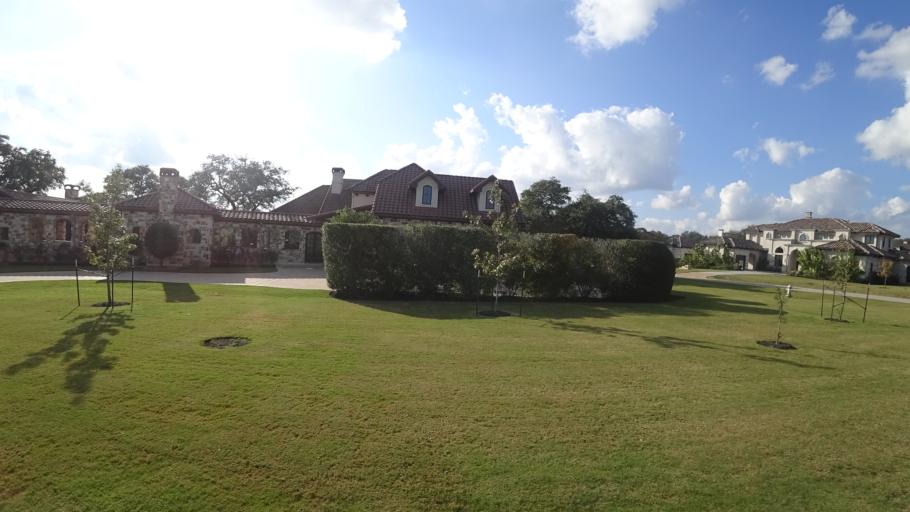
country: US
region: Texas
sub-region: Travis County
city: Barton Creek
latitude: 30.2786
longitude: -97.8770
